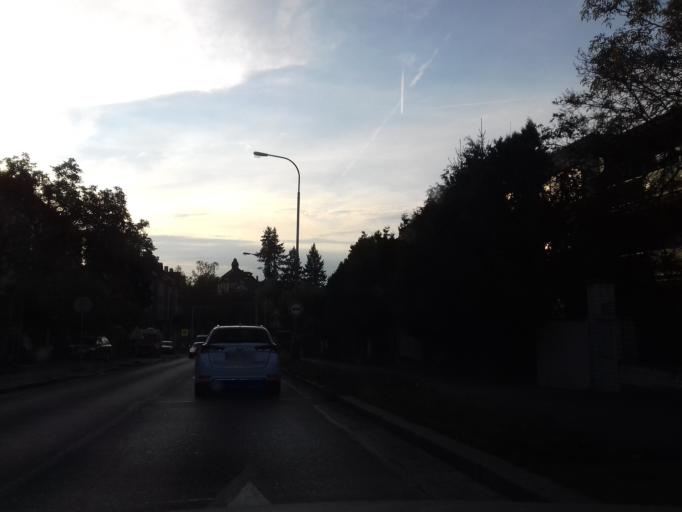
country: CZ
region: Praha
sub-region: Praha 4
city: Hodkovicky
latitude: 50.0311
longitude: 14.4491
